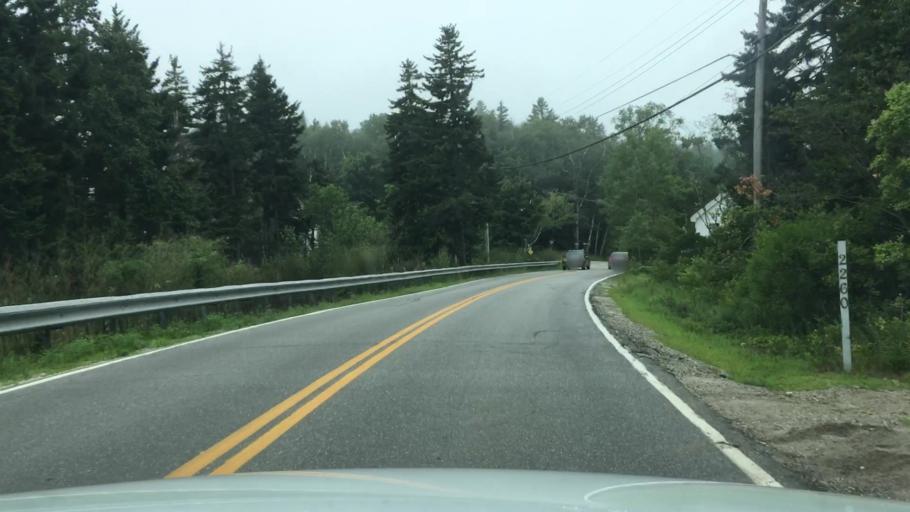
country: US
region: Maine
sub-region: Cumberland County
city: Harpswell Center
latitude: 43.7263
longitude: -69.9974
